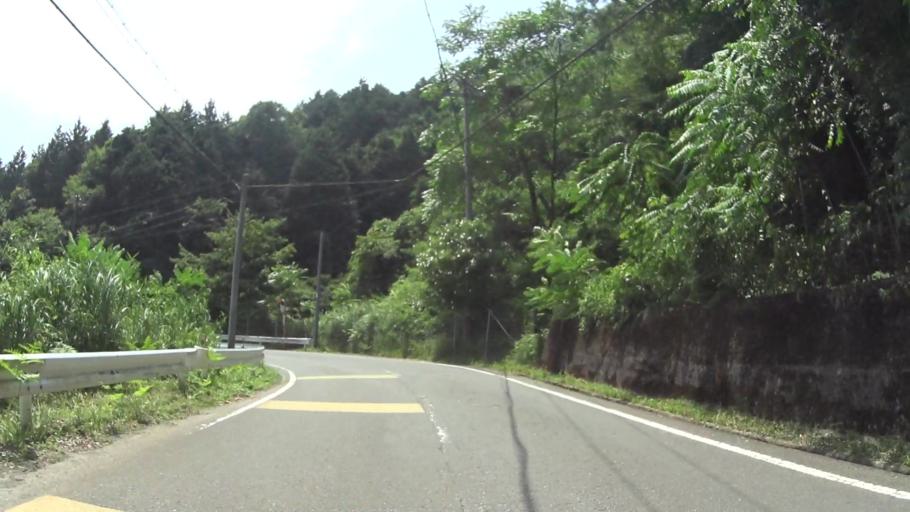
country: JP
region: Kyoto
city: Ayabe
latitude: 35.2793
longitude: 135.4312
